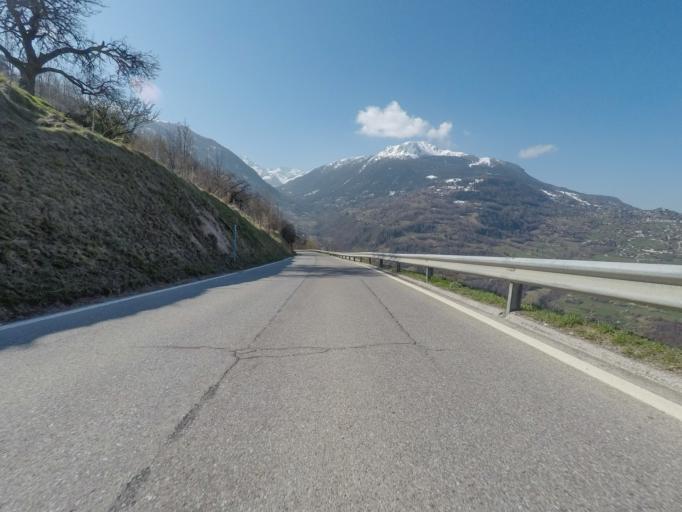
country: CH
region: Valais
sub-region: Conthey District
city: Basse-Nendaz
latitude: 46.1971
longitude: 7.3328
